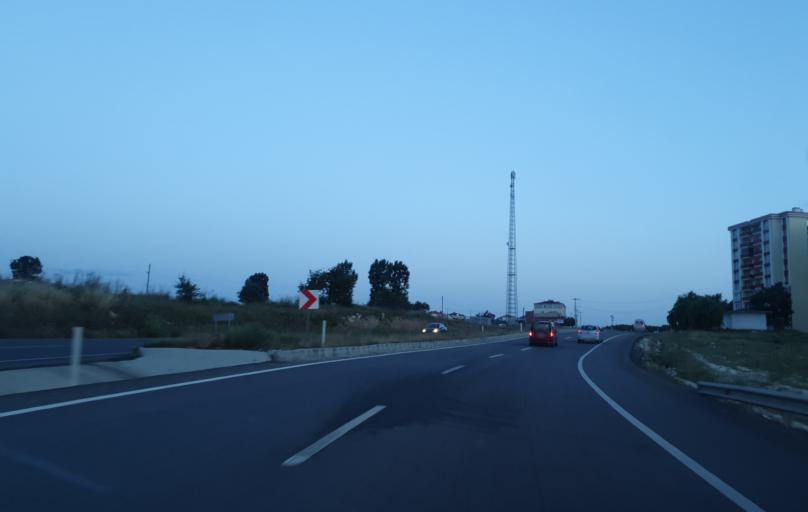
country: TR
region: Tekirdag
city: Saray
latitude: 41.3681
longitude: 27.9417
